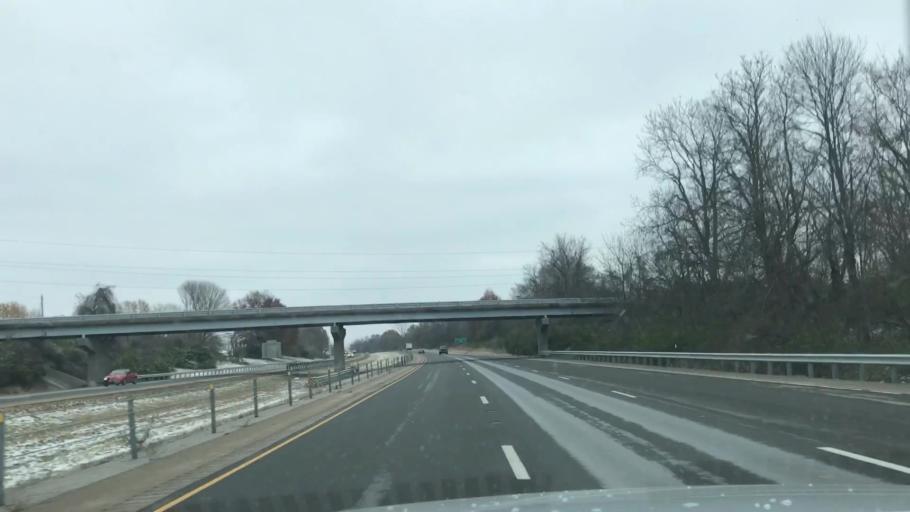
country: US
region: Illinois
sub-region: Madison County
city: Glen Carbon
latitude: 38.7546
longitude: -89.9529
